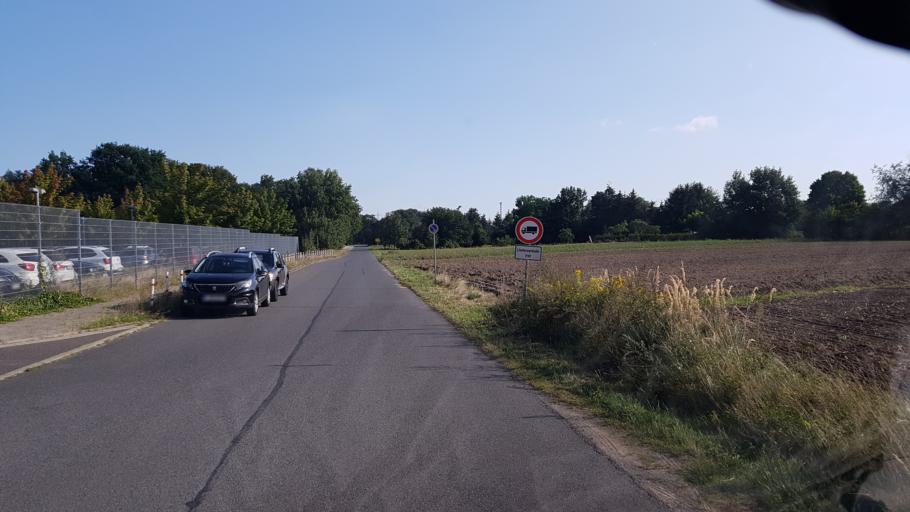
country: DE
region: Brandenburg
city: Luebben
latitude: 51.8942
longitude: 13.8044
